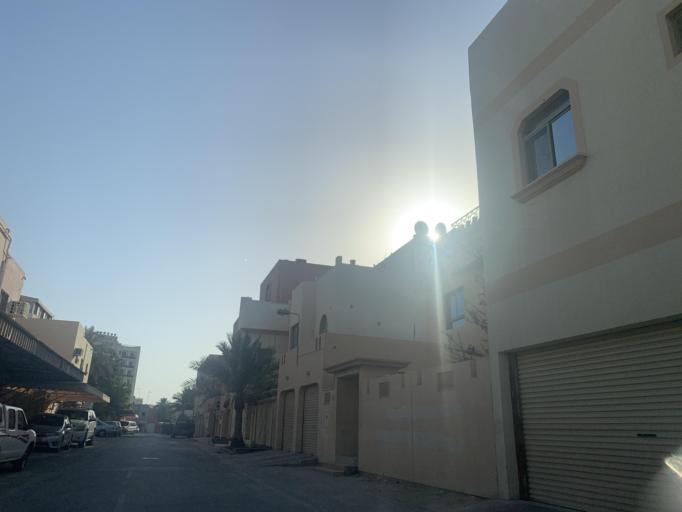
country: BH
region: Northern
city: Madinat `Isa
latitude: 26.1920
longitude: 50.4844
